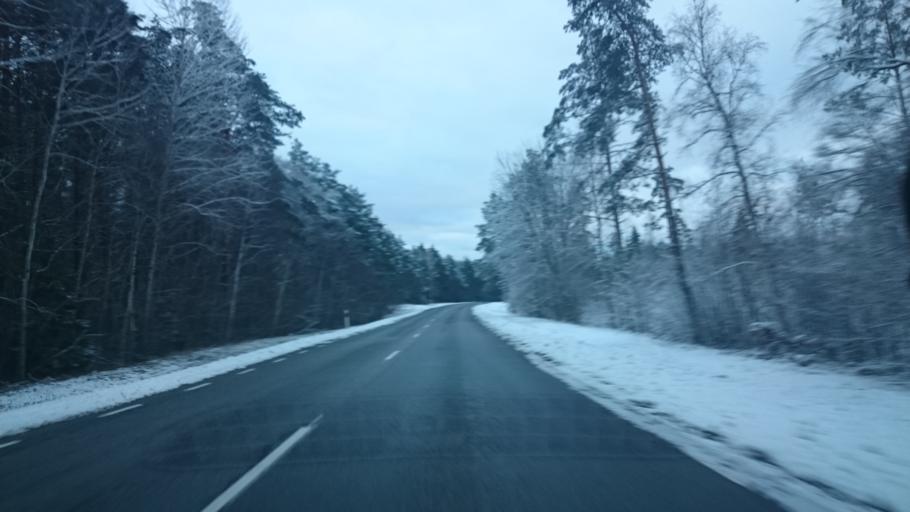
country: EE
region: Saare
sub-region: Kuressaare linn
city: Kuressaare
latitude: 58.3955
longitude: 22.6459
